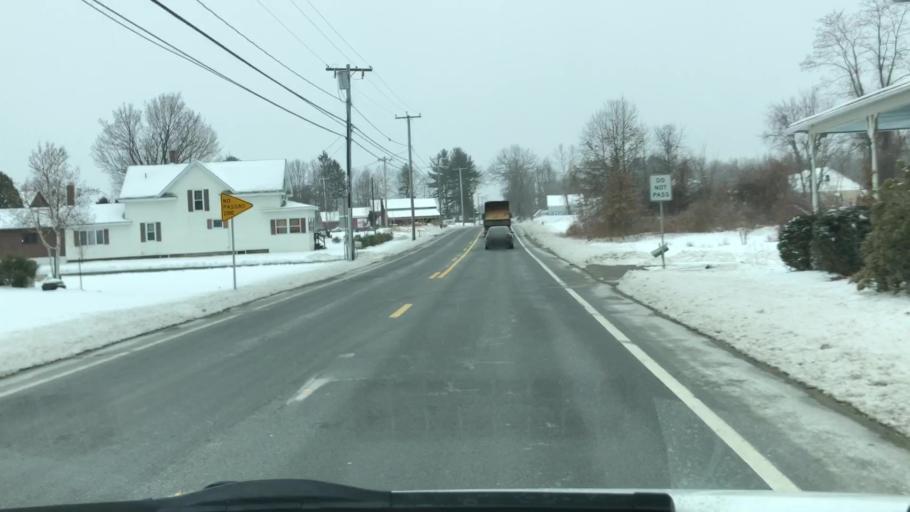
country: US
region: Massachusetts
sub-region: Franklin County
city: Whately
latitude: 42.4101
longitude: -72.6232
